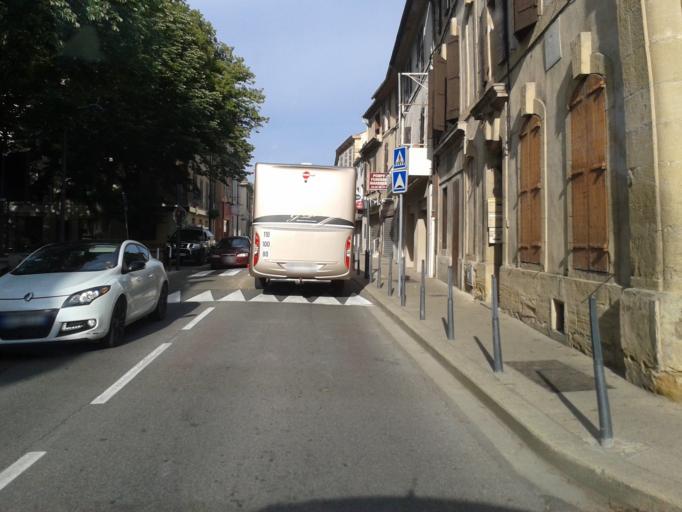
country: FR
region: Provence-Alpes-Cote d'Azur
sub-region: Departement des Bouches-du-Rhone
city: Peyrolles-en-Provence
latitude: 43.6464
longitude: 5.5823
